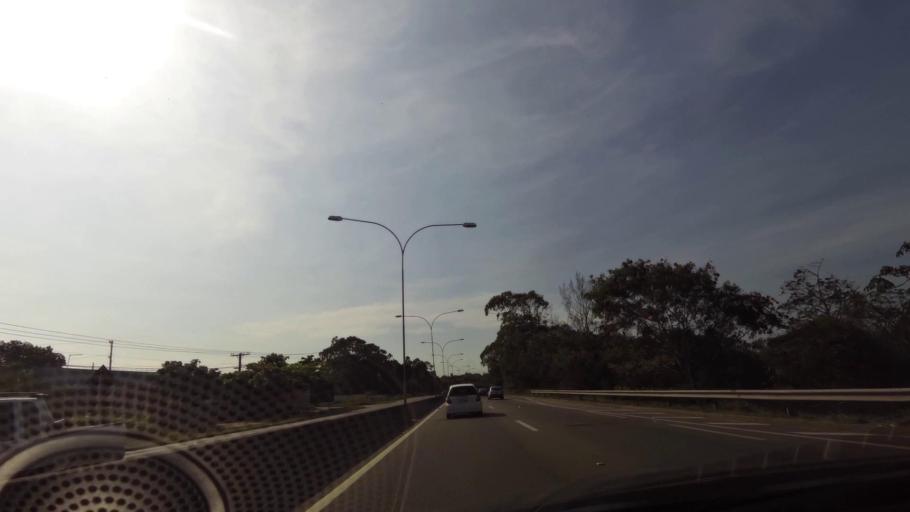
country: BR
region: Espirito Santo
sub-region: Viana
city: Viana
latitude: -20.5054
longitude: -40.3642
